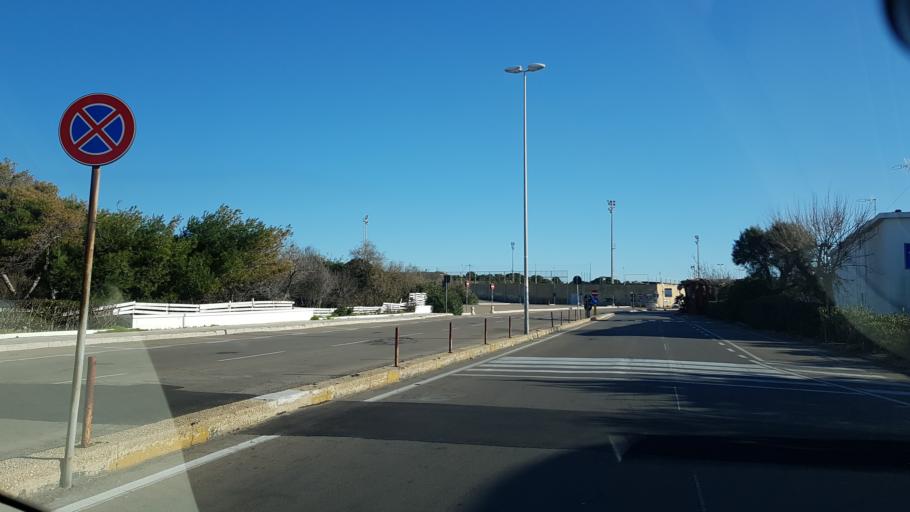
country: IT
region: Apulia
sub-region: Provincia di Lecce
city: Gallipoli
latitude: 40.0476
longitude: 18.0045
